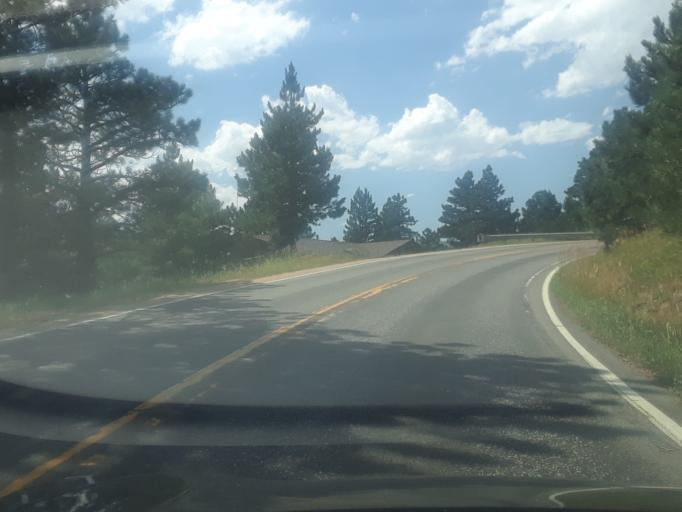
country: US
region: Colorado
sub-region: Boulder County
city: Boulder
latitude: 40.0310
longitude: -105.3220
